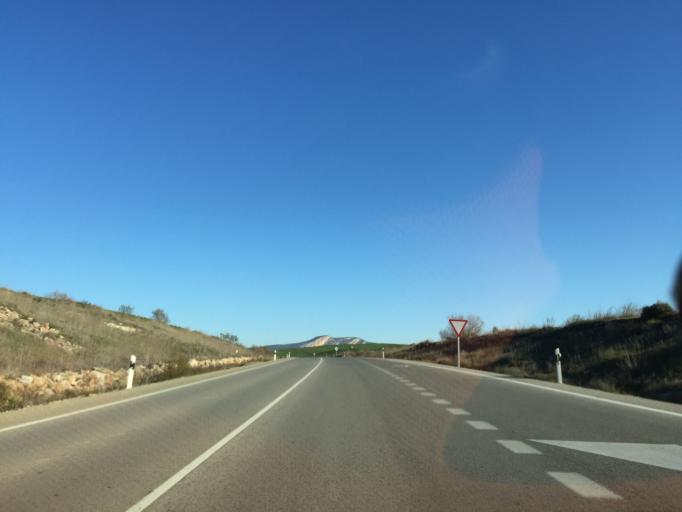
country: ES
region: Andalusia
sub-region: Provincia de Malaga
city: Ardales
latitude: 36.9149
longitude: -4.8417
